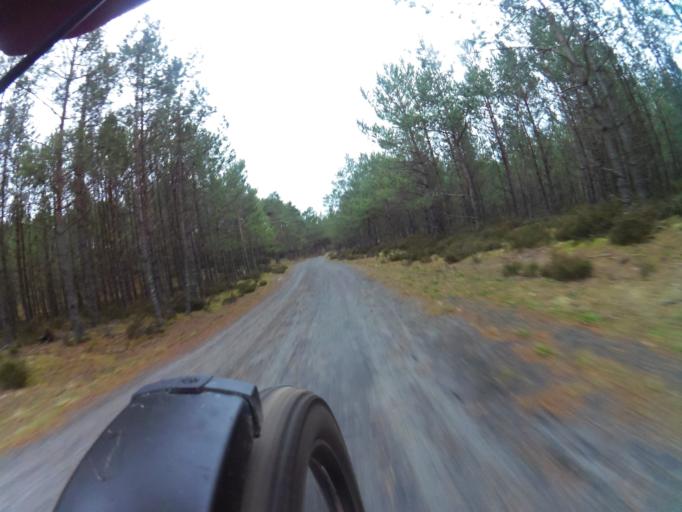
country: PL
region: Pomeranian Voivodeship
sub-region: Powiat wejherowski
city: Choczewo
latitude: 54.7869
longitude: 17.7471
